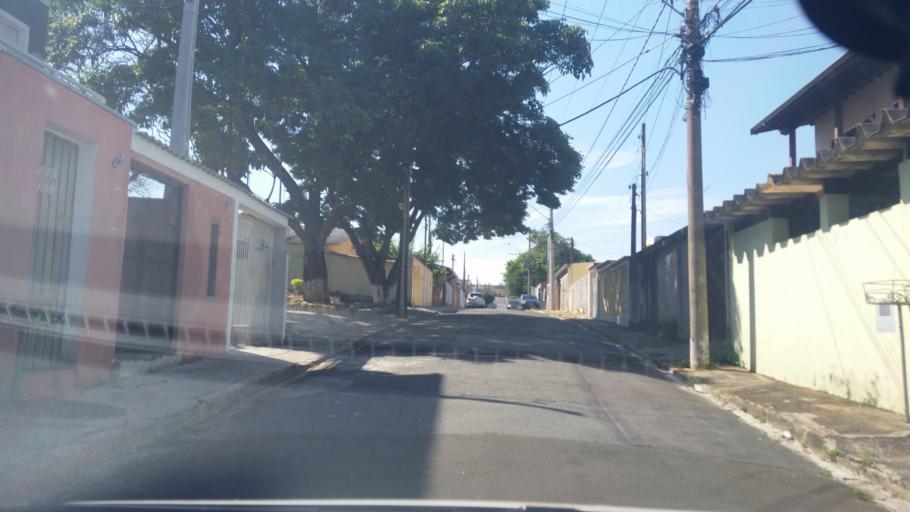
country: BR
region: Sao Paulo
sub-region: Campinas
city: Campinas
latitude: -22.8565
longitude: -47.0677
